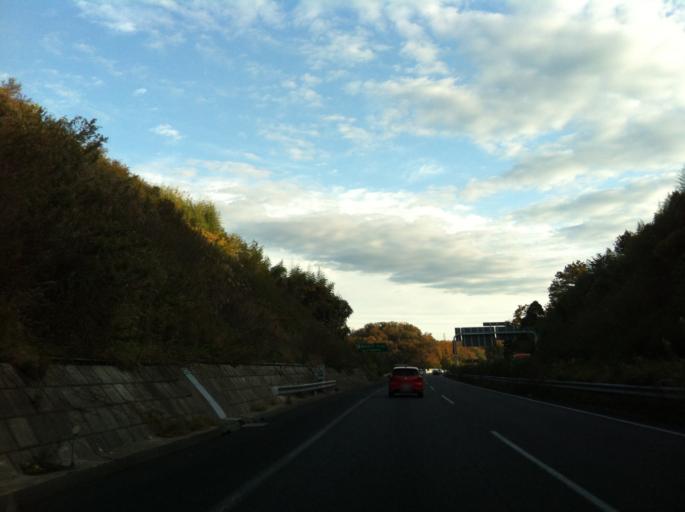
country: JP
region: Aichi
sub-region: Toyota-shi
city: Toyota
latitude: 35.0517
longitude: 137.1968
